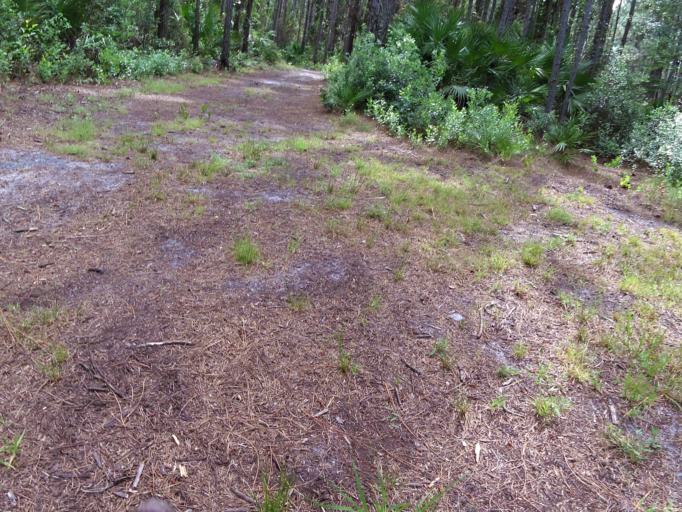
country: US
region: Florida
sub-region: Duval County
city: Atlantic Beach
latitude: 30.4570
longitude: -81.4693
